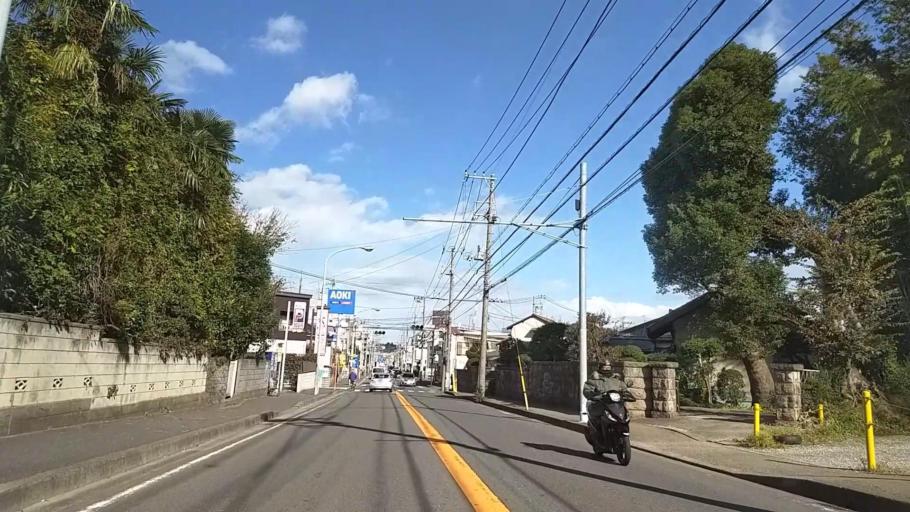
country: JP
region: Kanagawa
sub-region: Kawasaki-shi
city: Kawasaki
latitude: 35.5385
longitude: 139.6374
